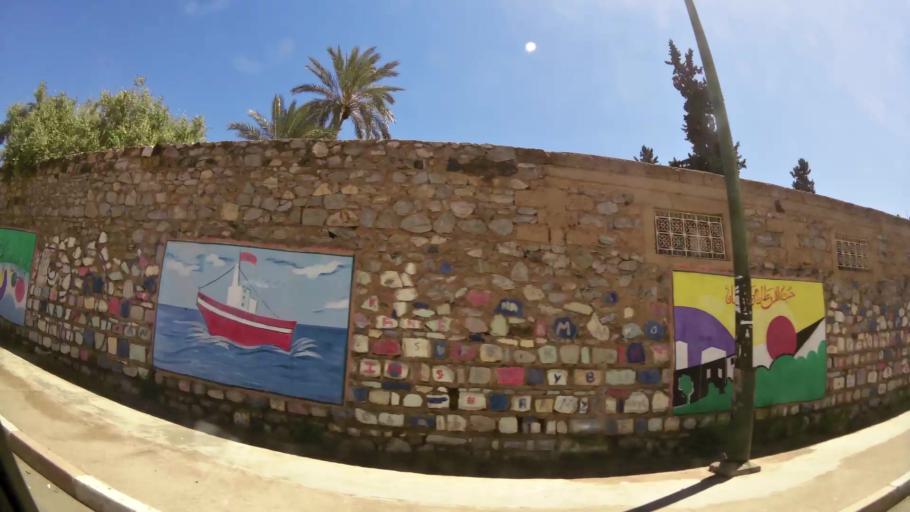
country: MA
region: Marrakech-Tensift-Al Haouz
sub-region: Marrakech
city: Marrakesh
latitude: 31.6478
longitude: -7.9905
